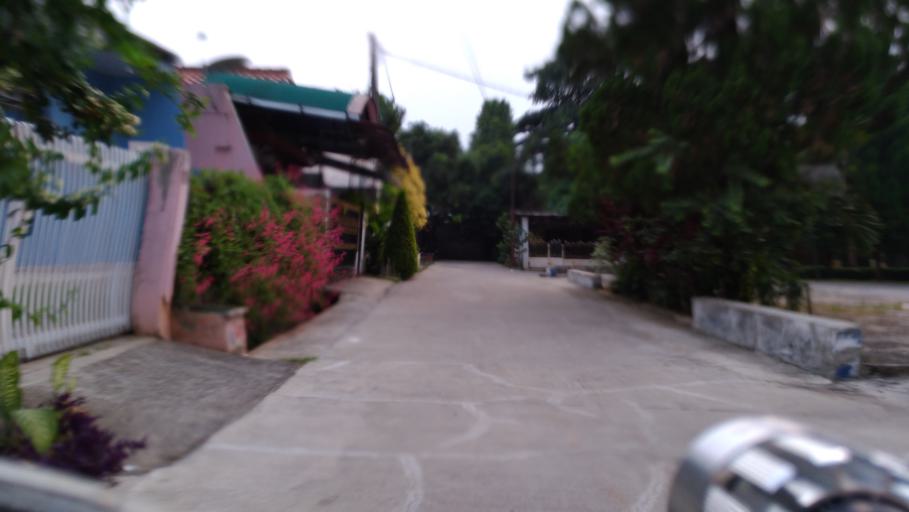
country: ID
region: West Java
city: Depok
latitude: -6.3645
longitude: 106.8624
